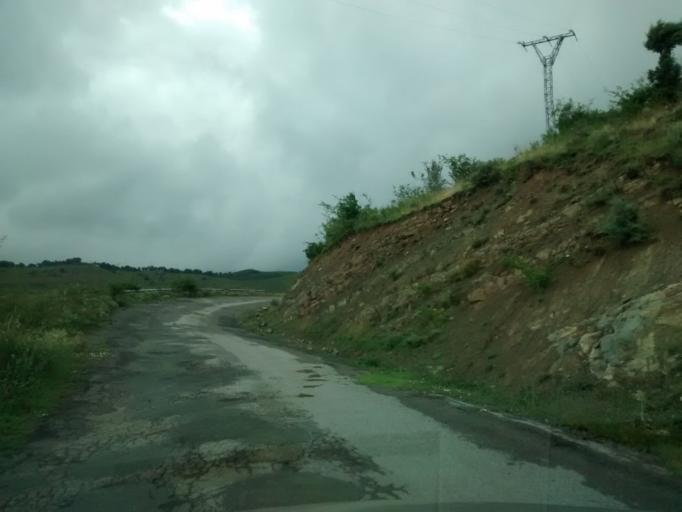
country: ES
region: La Rioja
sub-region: Provincia de La Rioja
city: San Roman de Cameros
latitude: 42.2177
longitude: -2.4576
